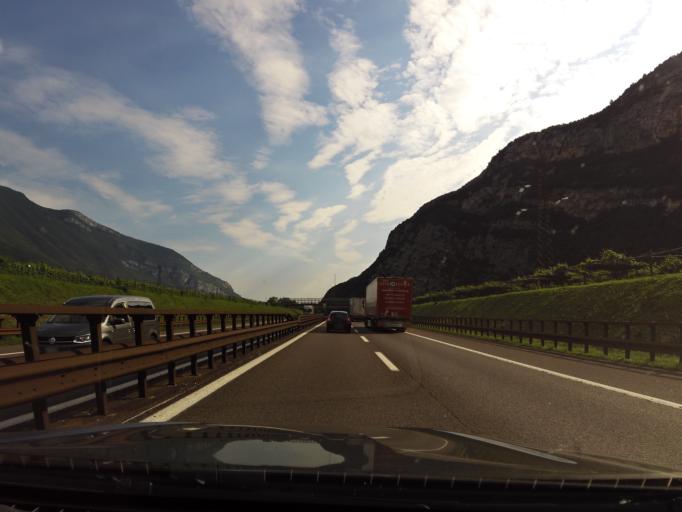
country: IT
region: Veneto
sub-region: Provincia di Verona
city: Dolce
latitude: 45.6171
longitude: 10.8572
